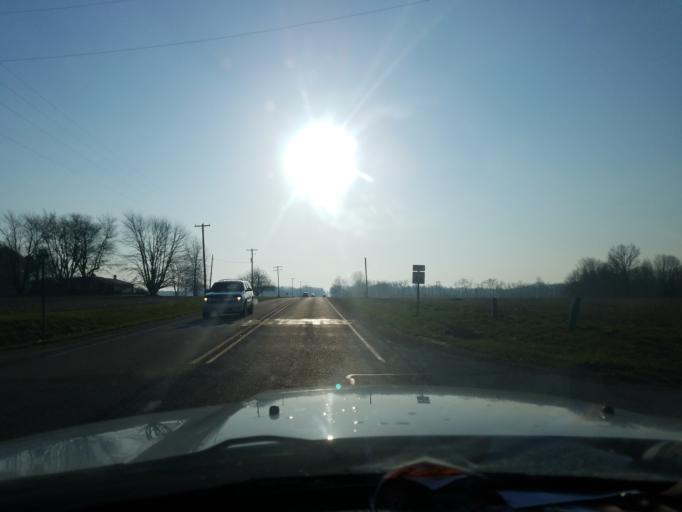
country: US
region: Indiana
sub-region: Vigo County
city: Seelyville
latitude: 39.3902
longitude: -87.2399
